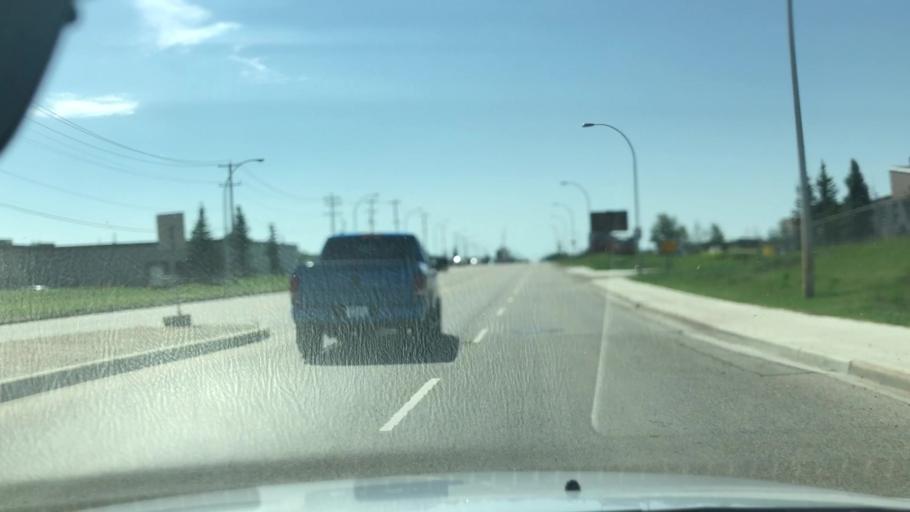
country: CA
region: Alberta
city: St. Albert
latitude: 53.5852
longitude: -113.5778
